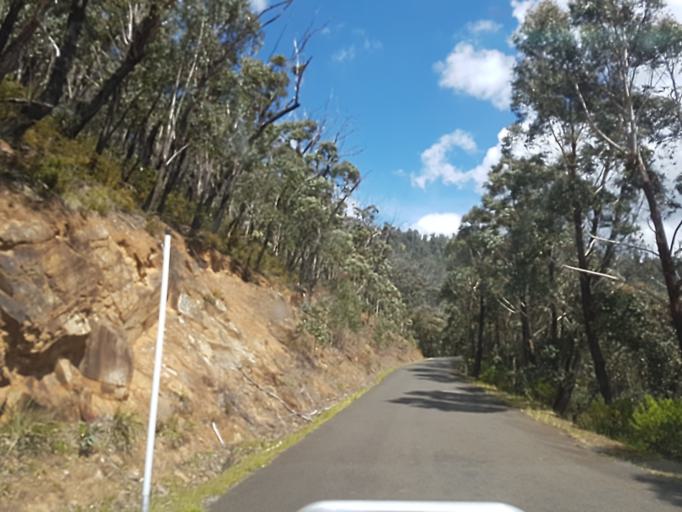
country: AU
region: Victoria
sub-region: East Gippsland
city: Bairnsdale
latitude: -37.3887
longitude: 147.2315
